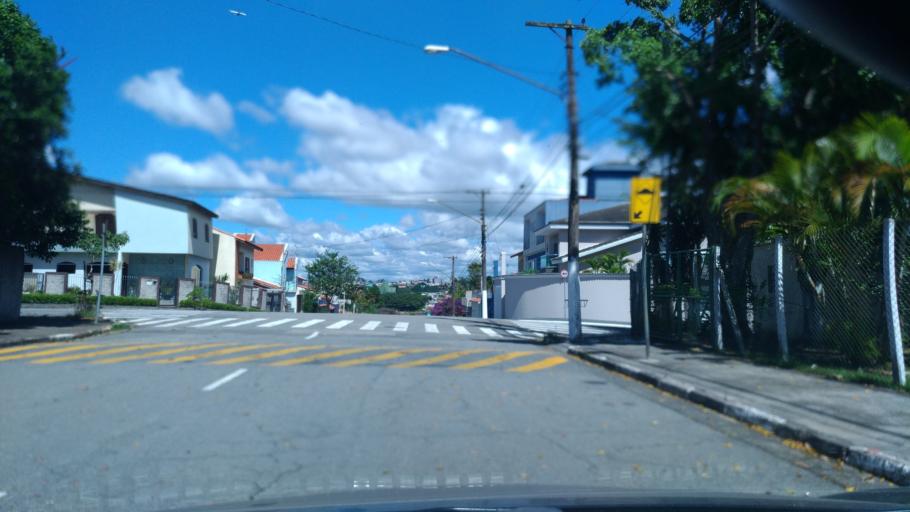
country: BR
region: Sao Paulo
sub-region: Sao Bernardo Do Campo
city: Sao Bernardo do Campo
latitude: -23.7095
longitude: -46.5825
